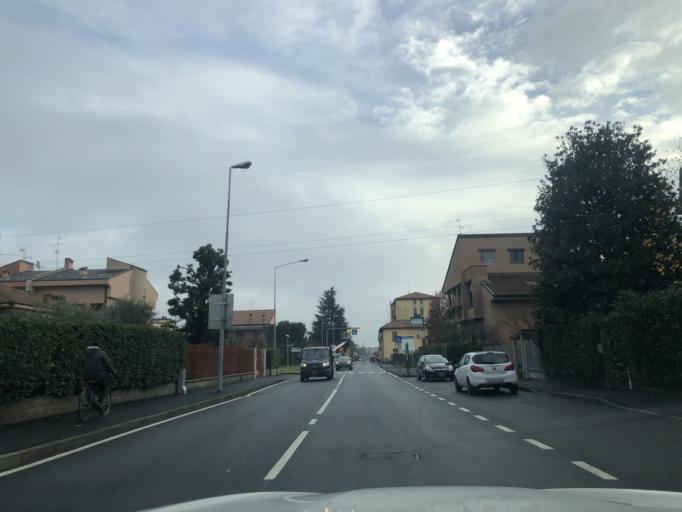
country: IT
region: Lombardy
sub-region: Citta metropolitana di Milano
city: Cologno Monzese
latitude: 45.5482
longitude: 9.2796
